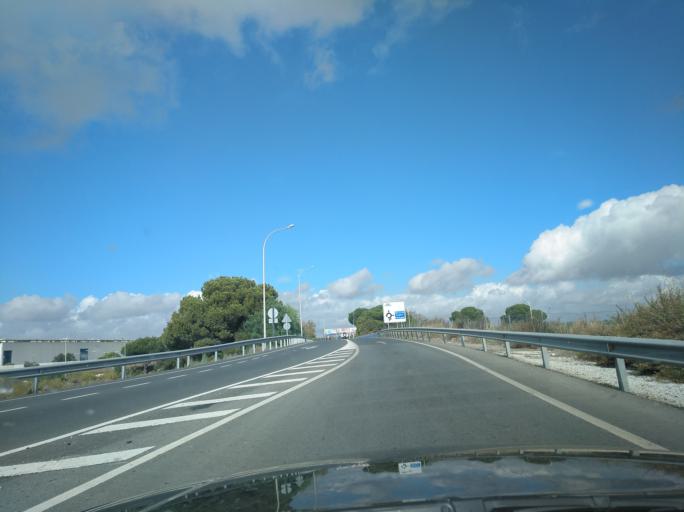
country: ES
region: Andalusia
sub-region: Provincia de Sevilla
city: Bollullos de la Mitacion
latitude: 37.3589
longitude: -6.1413
